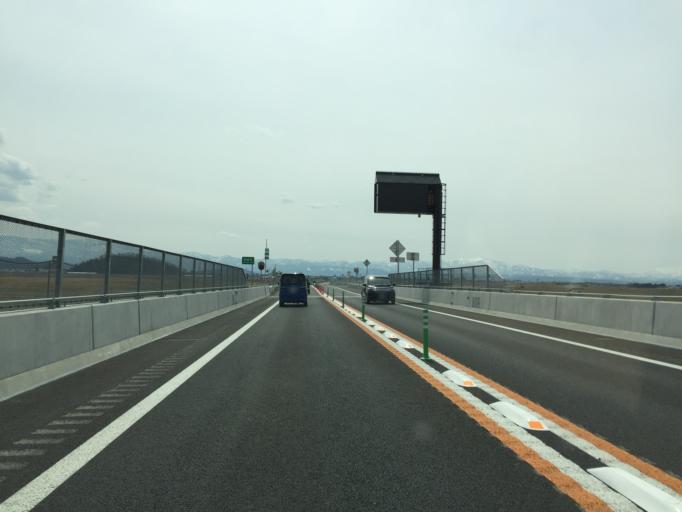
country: JP
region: Yamagata
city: Takahata
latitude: 38.0391
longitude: 140.1874
